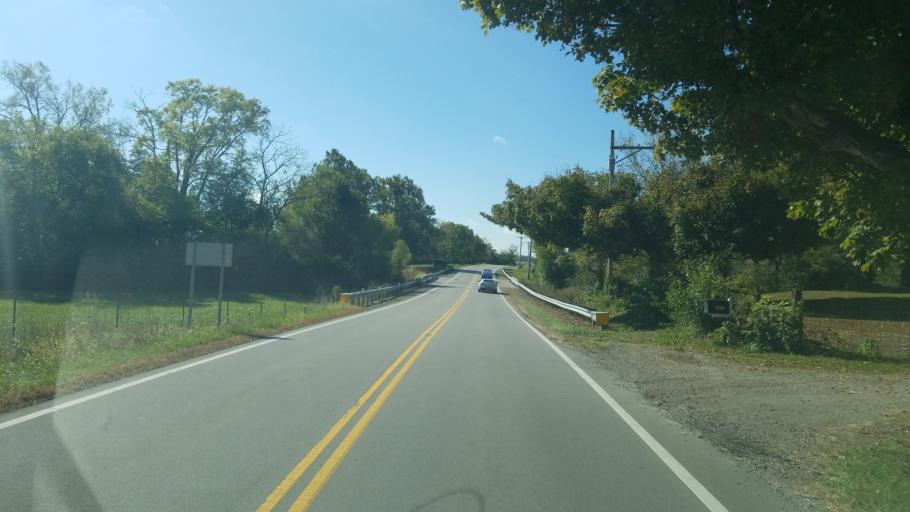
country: US
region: Ohio
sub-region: Fayette County
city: Washington Court House
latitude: 39.4739
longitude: -83.4841
